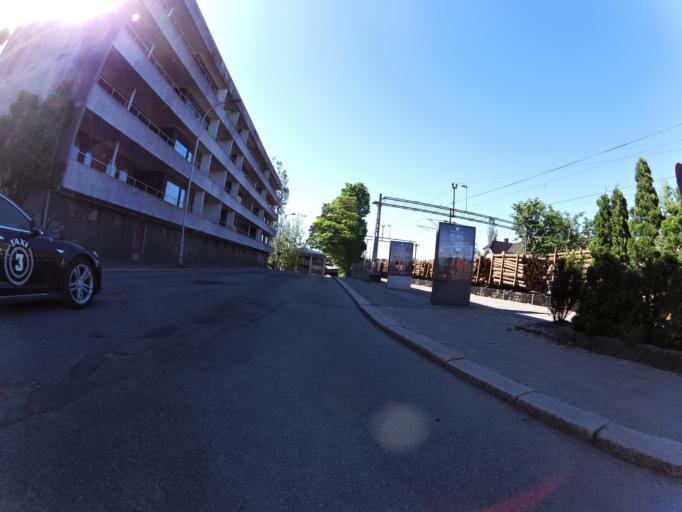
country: NO
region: Ostfold
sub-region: Fredrikstad
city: Fredrikstad
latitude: 59.2092
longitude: 10.9491
